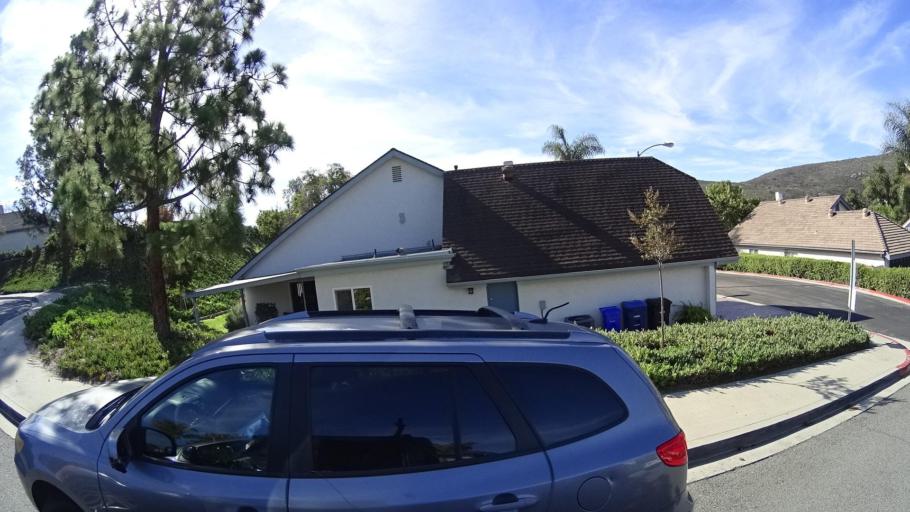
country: US
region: California
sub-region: San Diego County
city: Spring Valley
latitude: 32.7294
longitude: -116.9824
